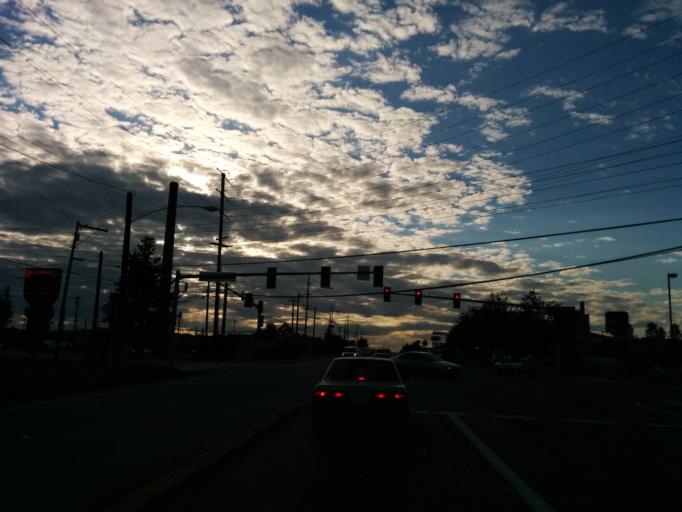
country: US
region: Washington
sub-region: Snohomish County
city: Monroe
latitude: 47.8578
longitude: -121.9637
